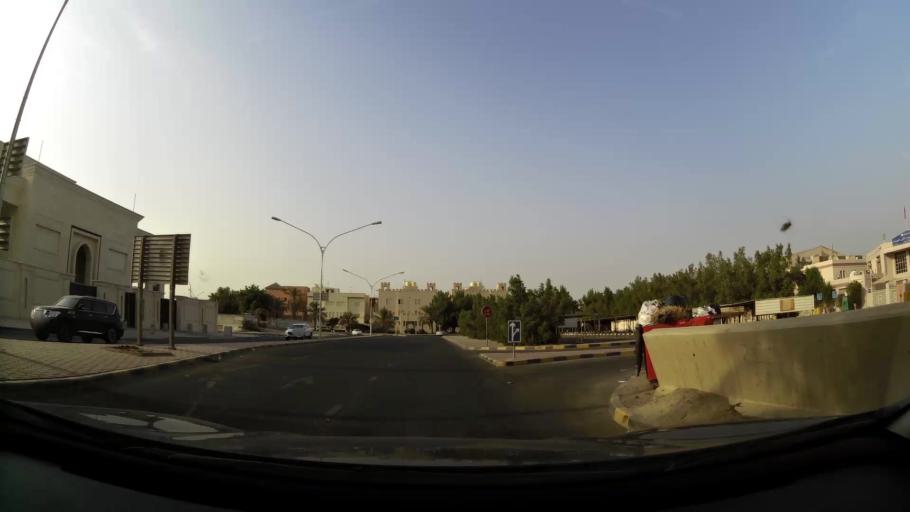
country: KW
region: Muhafazat Hawalli
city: Hawalli
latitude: 29.3140
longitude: 48.0320
